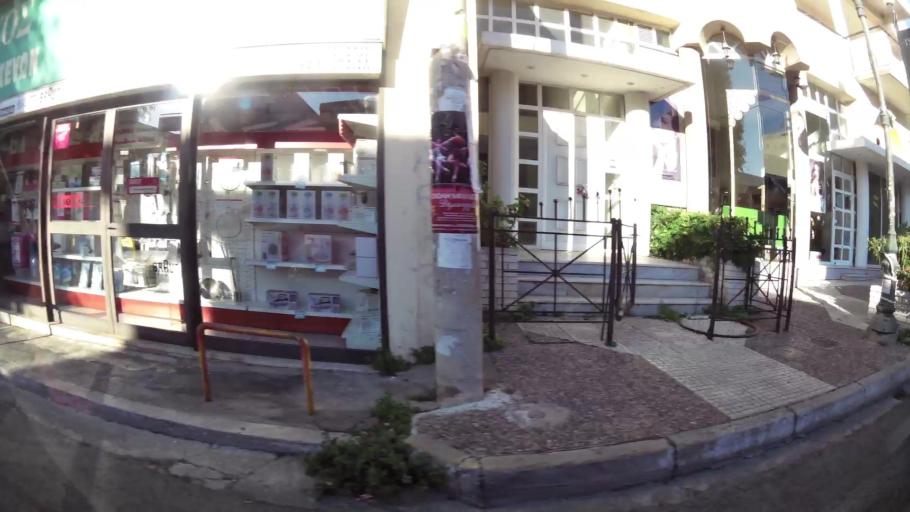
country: GR
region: Attica
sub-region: Nomarchia Anatolikis Attikis
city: Pallini
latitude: 38.0032
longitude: 23.8807
